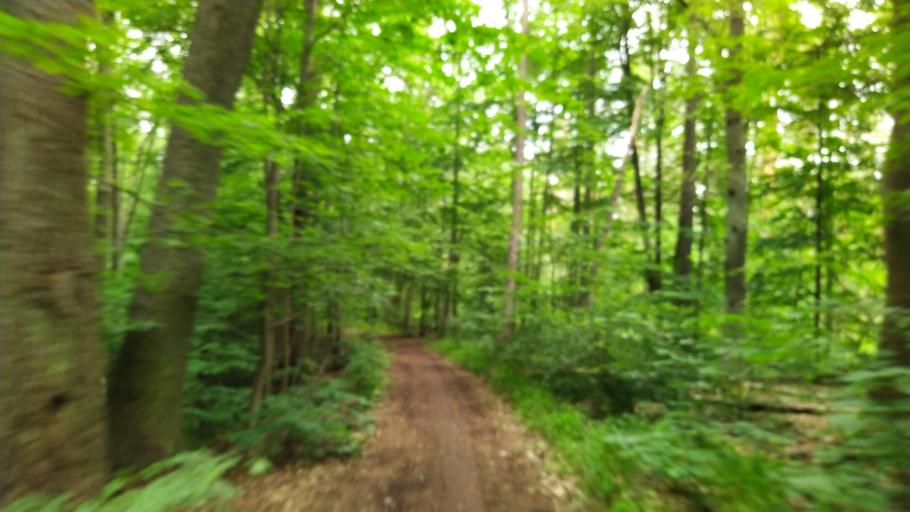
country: DE
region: Berlin
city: Falkenhagener Feld
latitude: 52.5783
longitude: 13.1649
